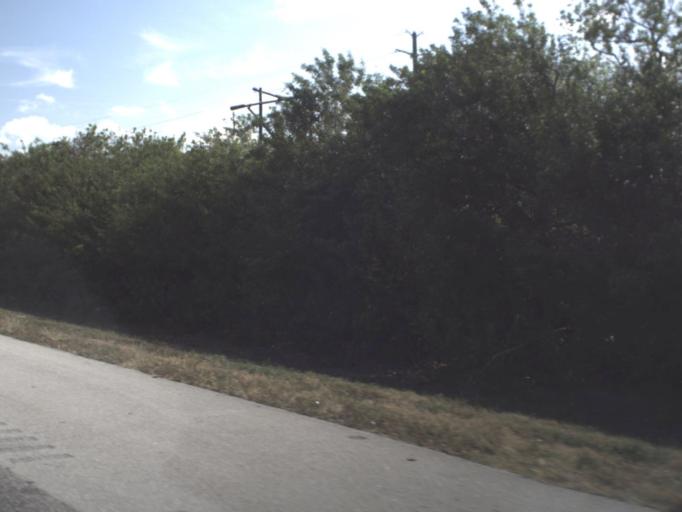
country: US
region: Florida
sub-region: Brevard County
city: June Park
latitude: 28.0957
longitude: -80.7062
